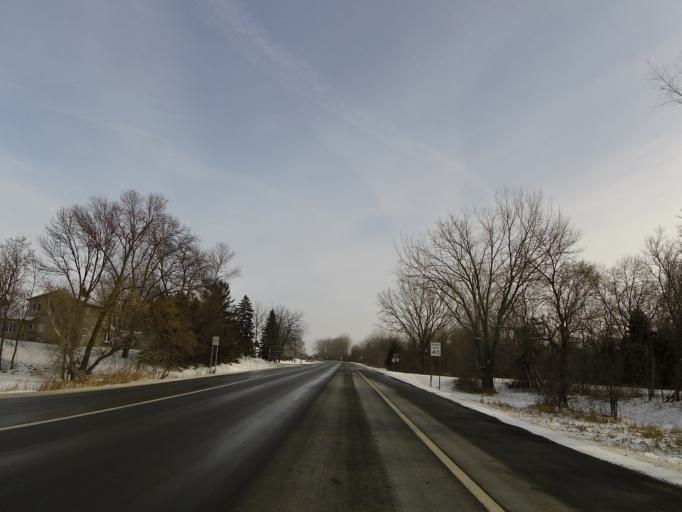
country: US
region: Minnesota
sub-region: McLeod County
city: Hutchinson
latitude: 44.8927
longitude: -94.4054
